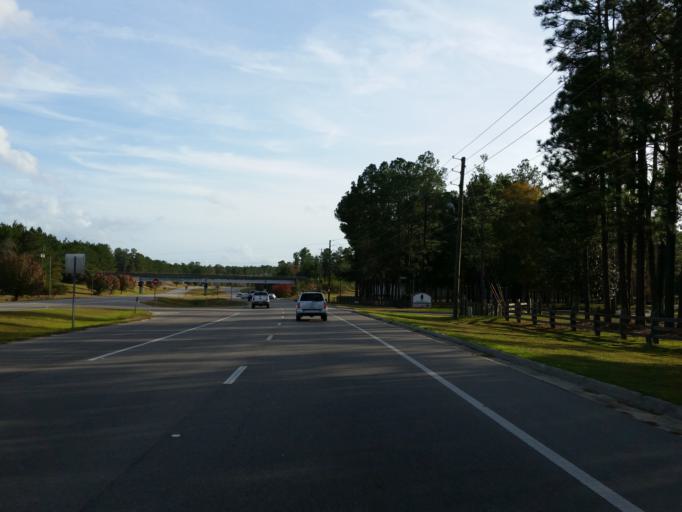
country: US
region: Mississippi
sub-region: Forrest County
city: Hattiesburg
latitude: 31.2954
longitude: -89.3241
